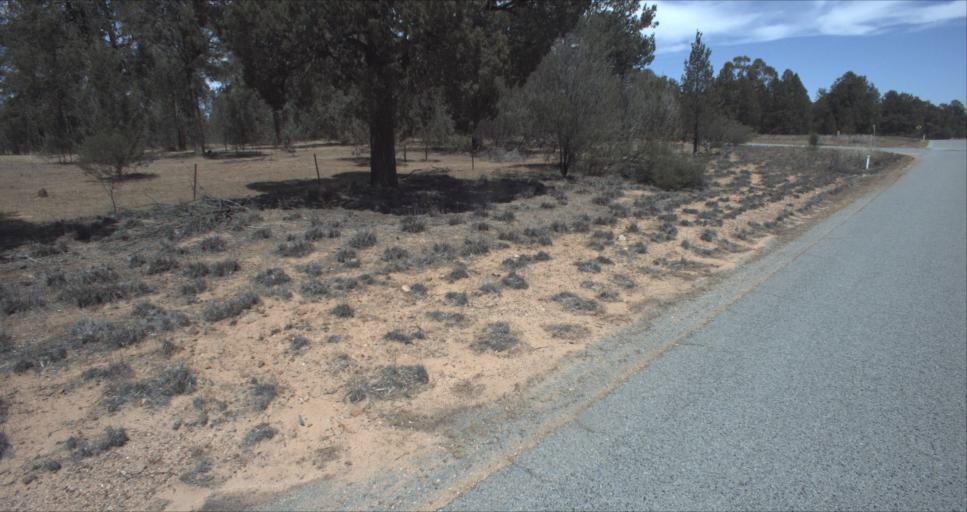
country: AU
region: New South Wales
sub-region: Leeton
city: Leeton
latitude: -34.6702
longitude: 146.4444
